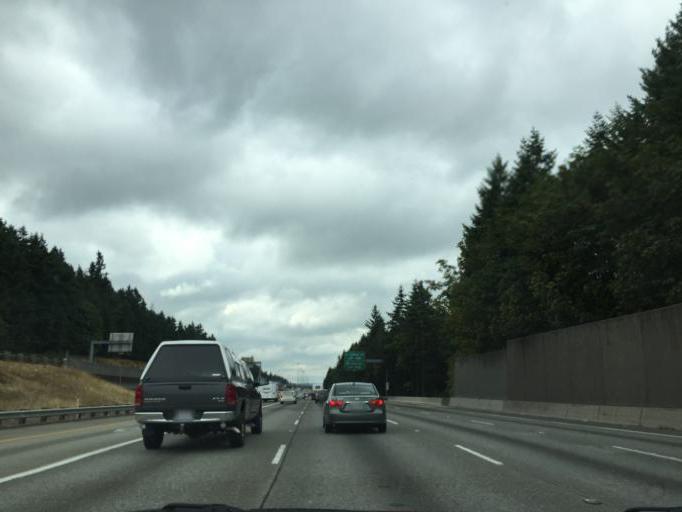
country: US
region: Washington
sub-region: King County
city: Federal Way
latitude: 47.3013
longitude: -122.3029
